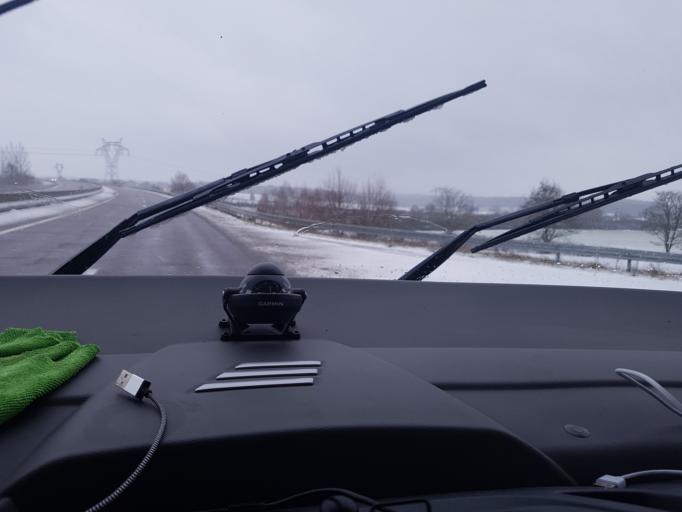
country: FR
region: Lorraine
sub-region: Departement de la Moselle
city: Peltre
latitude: 49.0751
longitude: 6.2401
